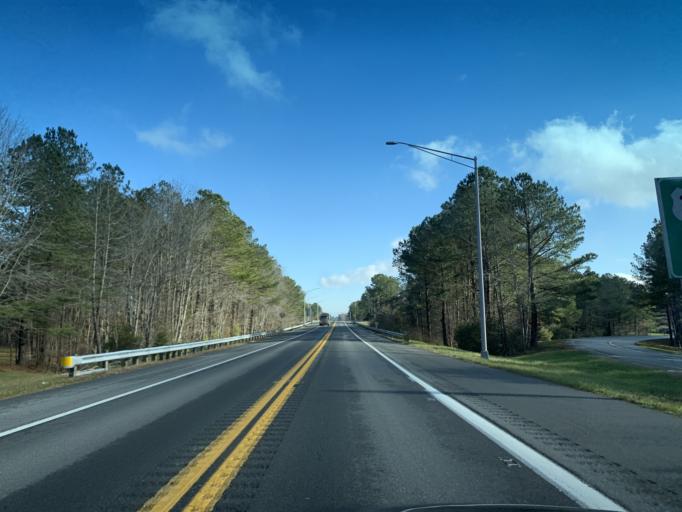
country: US
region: Maryland
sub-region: Worcester County
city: Berlin
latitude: 38.3771
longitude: -75.2104
